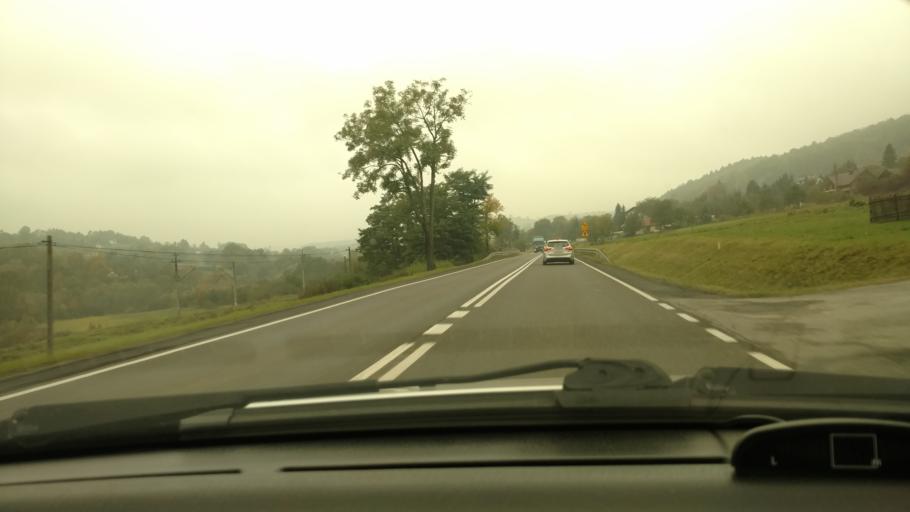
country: PL
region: Lesser Poland Voivodeship
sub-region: Powiat nowosadecki
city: Grybow
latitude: 49.6233
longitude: 20.9280
